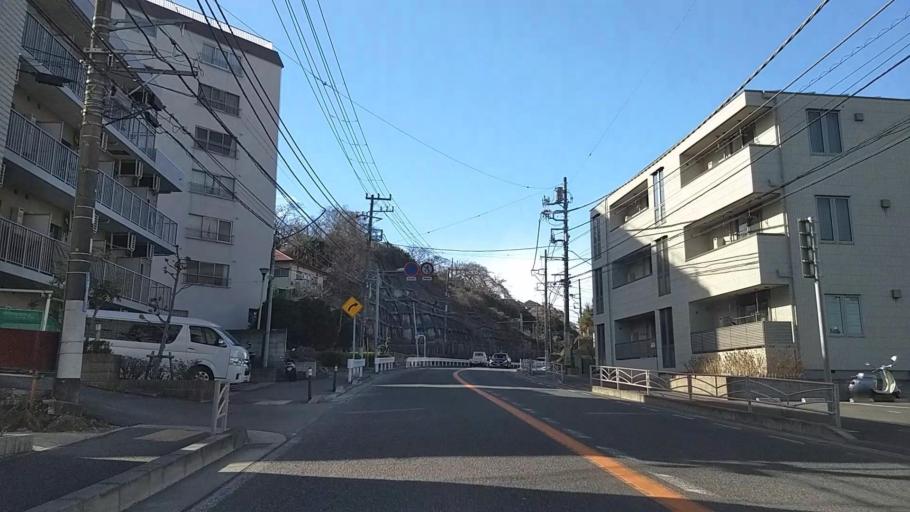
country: JP
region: Kanagawa
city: Yokohama
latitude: 35.3725
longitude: 139.6290
